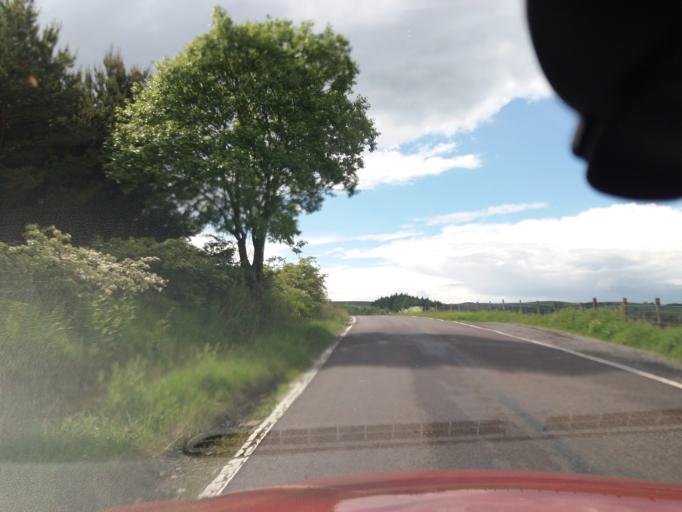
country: GB
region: England
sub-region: Blackburn with Darwen
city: Darwen
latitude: 53.6479
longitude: -2.4276
